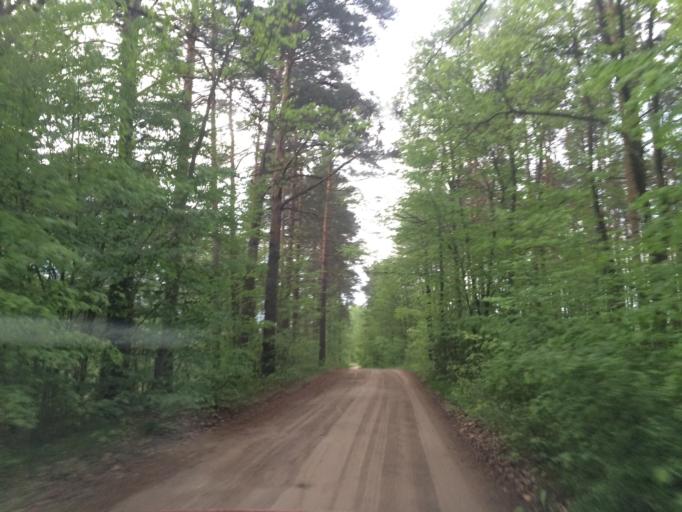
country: PL
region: Warmian-Masurian Voivodeship
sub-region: Powiat nowomiejski
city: Kurzetnik
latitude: 53.3612
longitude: 19.5182
